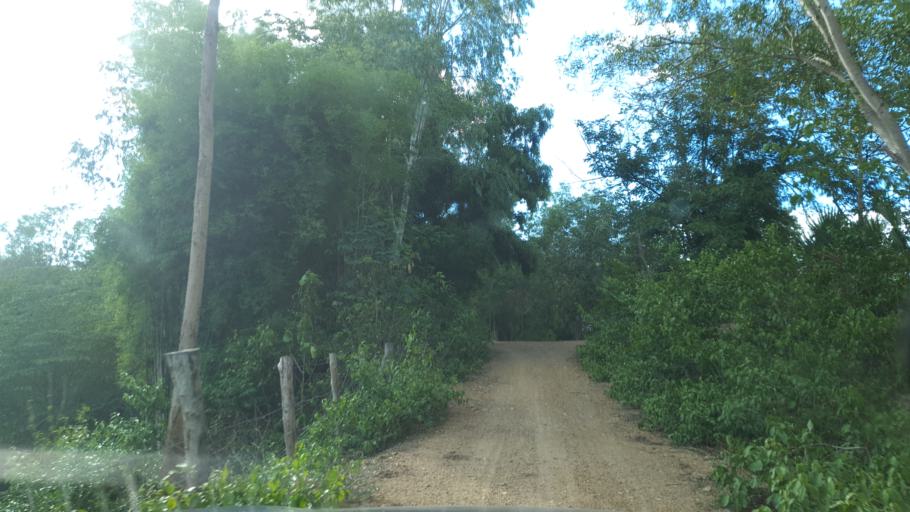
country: TH
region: Lampang
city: Sop Prap
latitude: 17.8819
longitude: 99.2940
